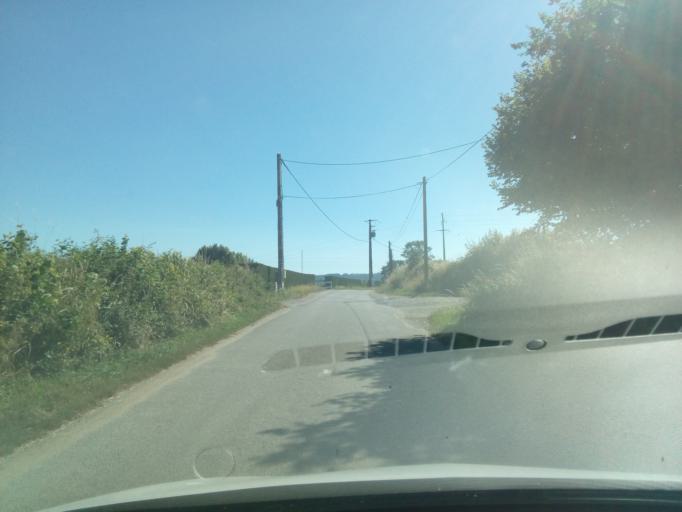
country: FR
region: Limousin
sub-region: Departement de la Creuse
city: Gueret
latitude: 46.2116
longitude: 1.8862
